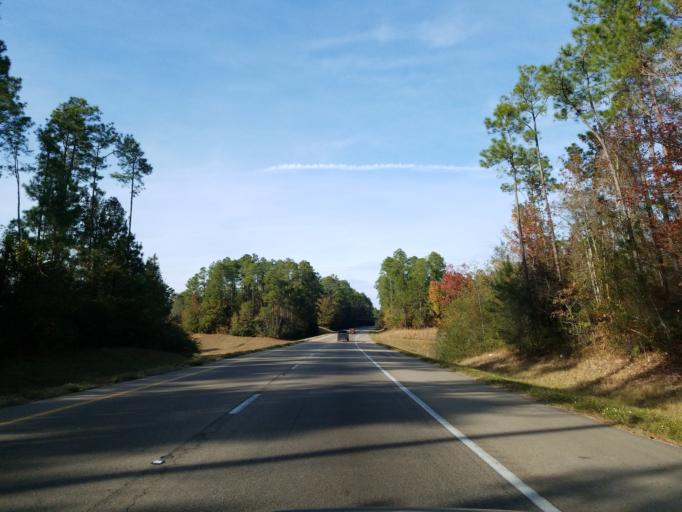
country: US
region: Mississippi
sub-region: Lamar County
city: West Hattiesburg
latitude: 31.2797
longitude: -89.3505
